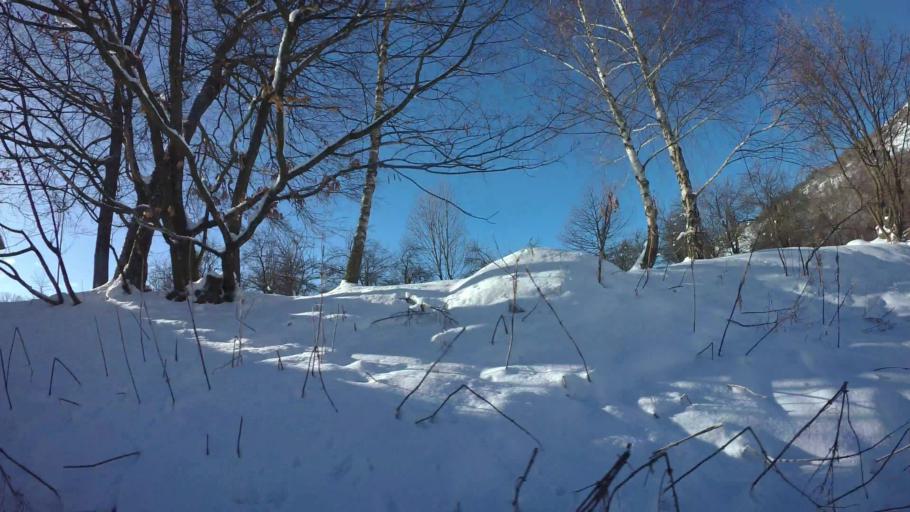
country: BA
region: Federation of Bosnia and Herzegovina
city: Kobilja Glava
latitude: 43.8974
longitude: 18.4146
